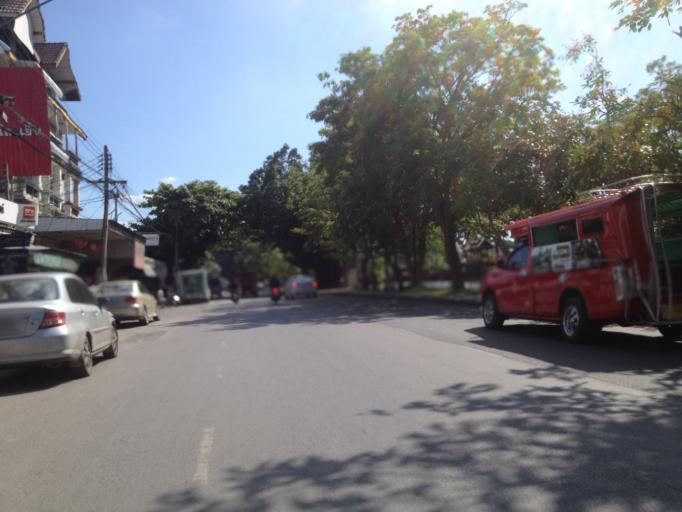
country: TH
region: Chiang Mai
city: Chiang Mai
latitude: 18.7911
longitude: 98.9784
